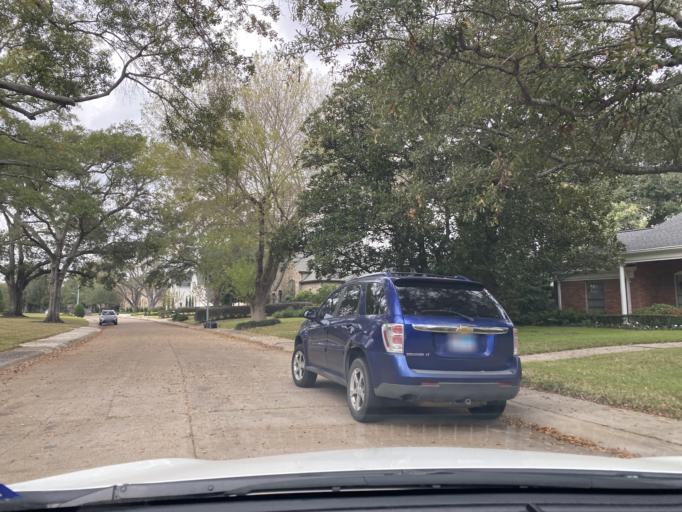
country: US
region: Texas
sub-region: Harris County
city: Hunters Creek Village
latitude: 29.7470
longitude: -95.4746
